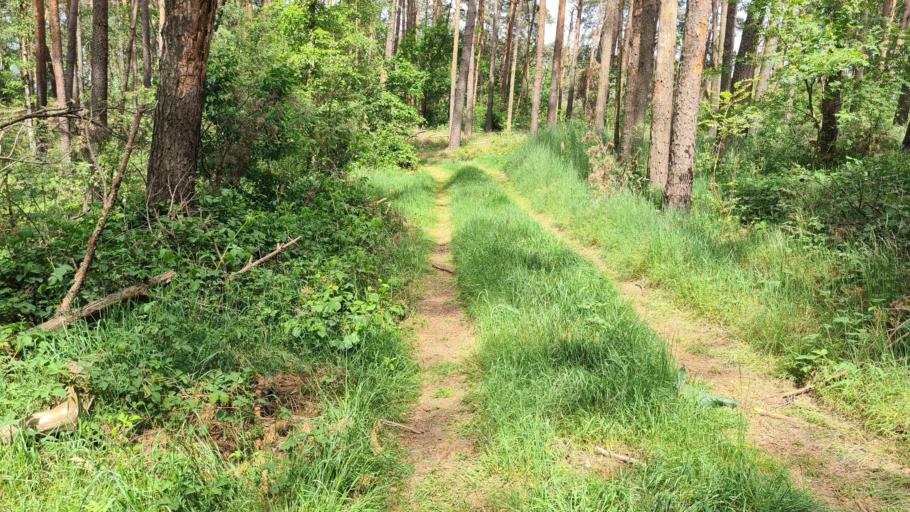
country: DE
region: Brandenburg
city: Grosskmehlen
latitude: 51.3697
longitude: 13.7068
